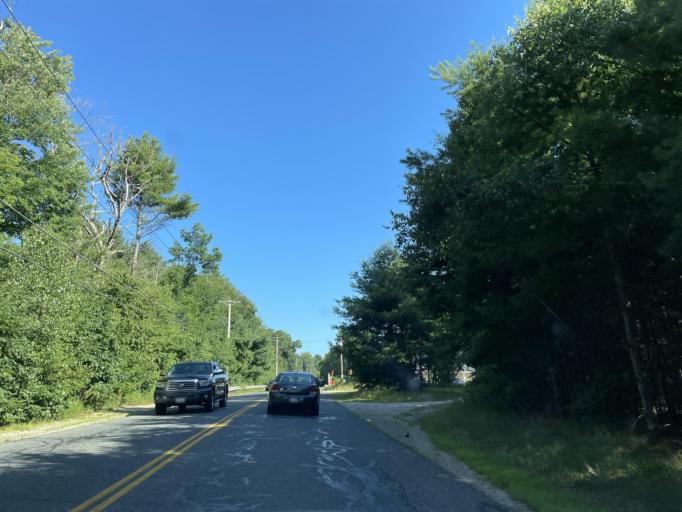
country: US
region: Massachusetts
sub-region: Worcester County
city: East Douglas
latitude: 42.0658
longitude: -71.6953
